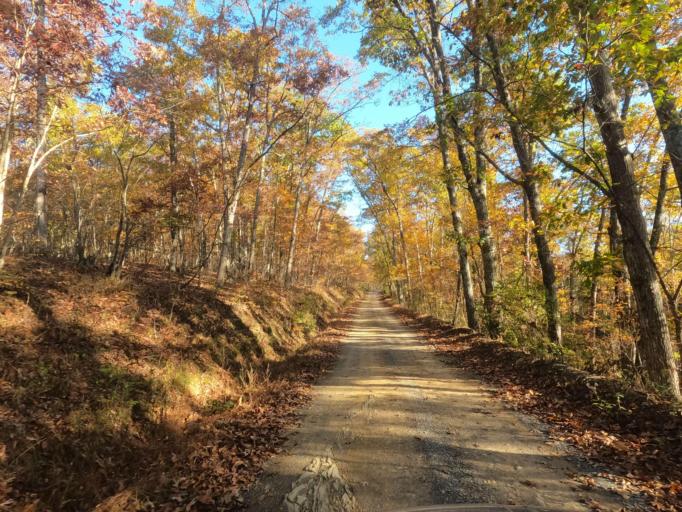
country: US
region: West Virginia
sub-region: Mineral County
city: Fort Ashby
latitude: 39.5306
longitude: -78.5374
